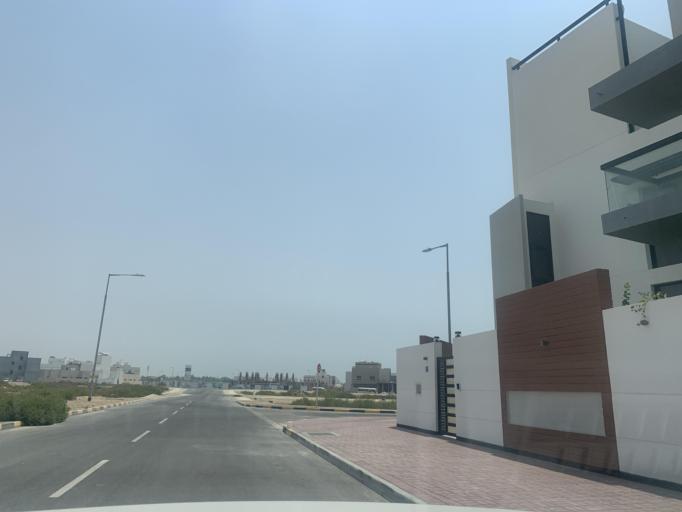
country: BH
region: Central Governorate
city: Madinat Hamad
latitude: 26.1334
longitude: 50.4700
